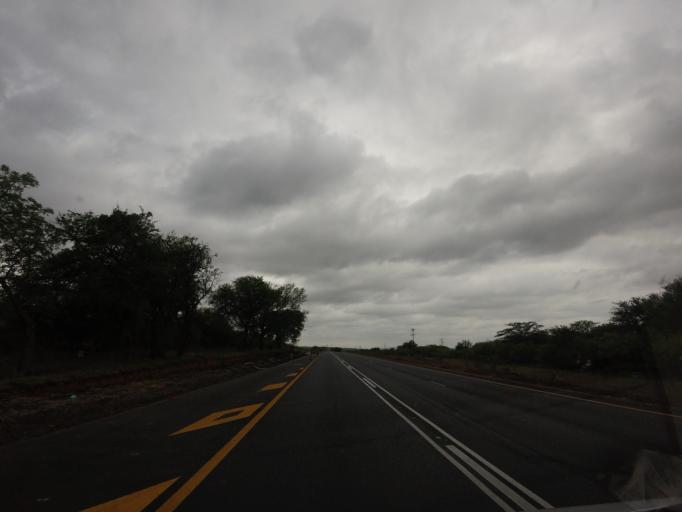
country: ZA
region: Mpumalanga
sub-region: Ehlanzeni District
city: Komatipoort
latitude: -25.4362
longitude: 31.8109
